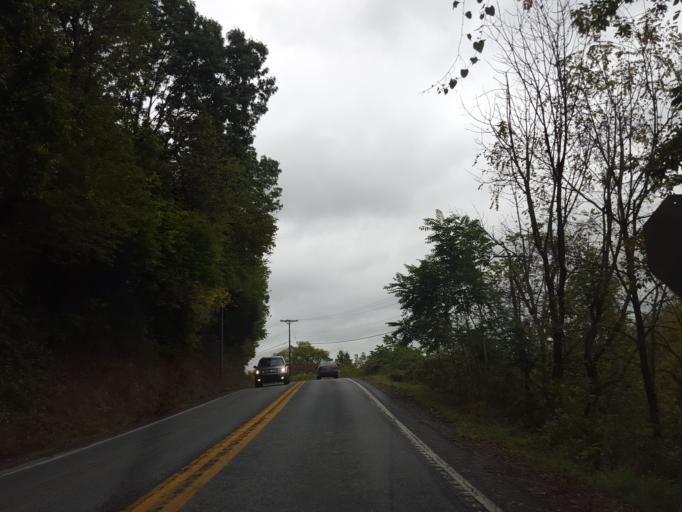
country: US
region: Pennsylvania
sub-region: York County
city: East York
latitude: 39.9472
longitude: -76.6659
